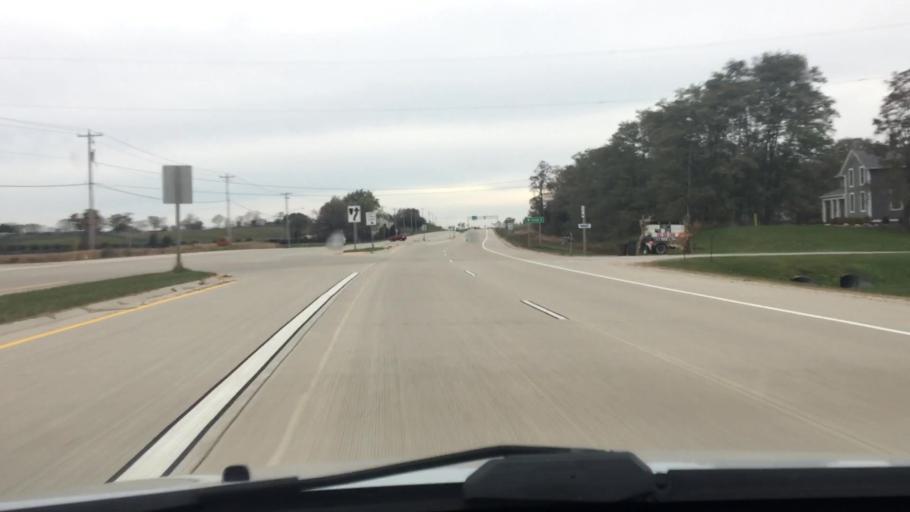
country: US
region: Wisconsin
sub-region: Waukesha County
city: North Prairie
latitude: 42.9283
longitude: -88.3464
